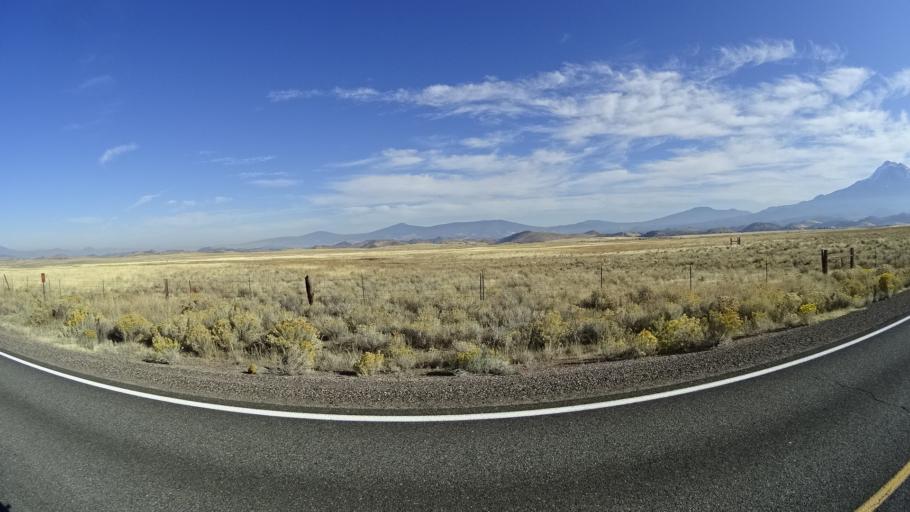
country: US
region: California
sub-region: Siskiyou County
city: Weed
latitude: 41.4809
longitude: -122.4948
